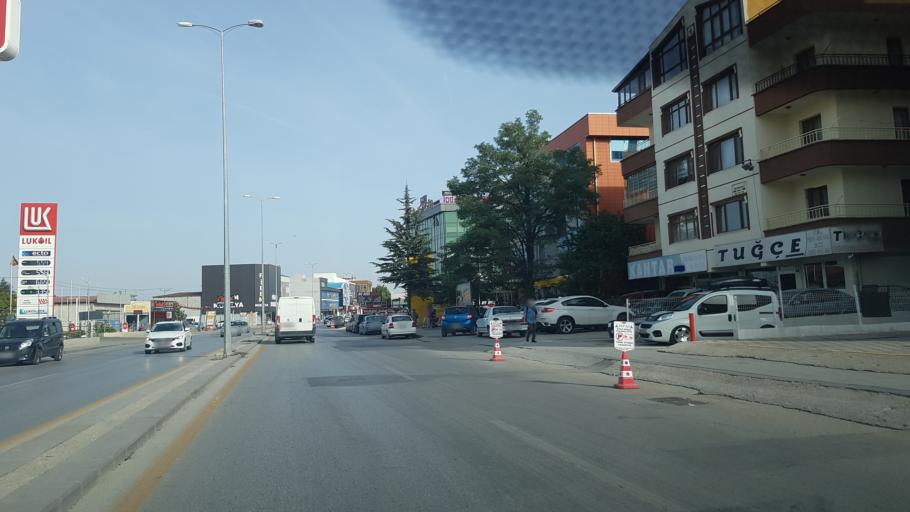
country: TR
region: Ankara
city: Etimesgut
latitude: 39.9527
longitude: 32.6399
